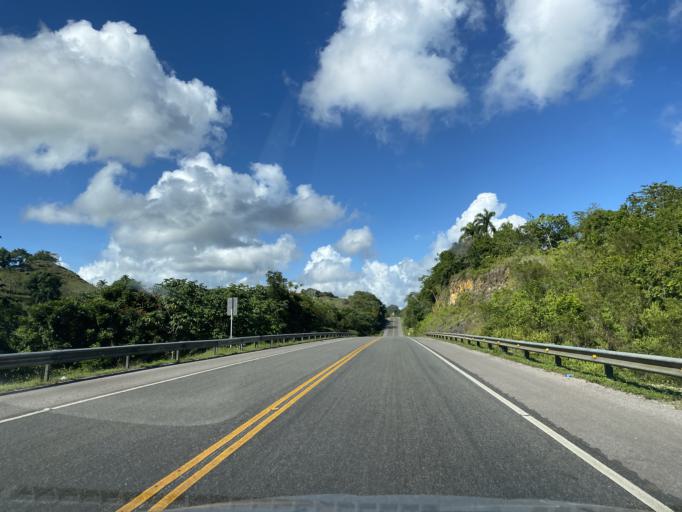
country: DO
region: Monte Plata
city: Majagual
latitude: 19.0327
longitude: -69.8262
